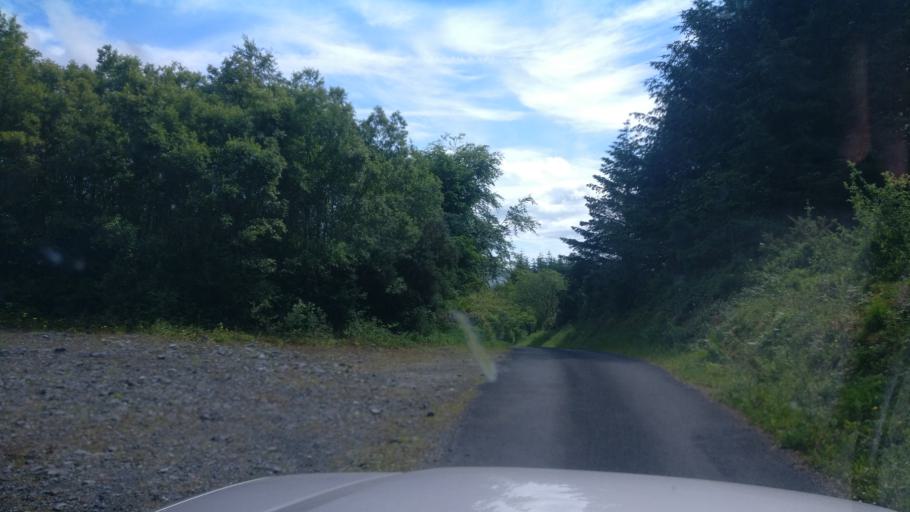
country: IE
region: Connaught
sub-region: County Galway
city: Gort
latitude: 53.0814
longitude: -8.7097
